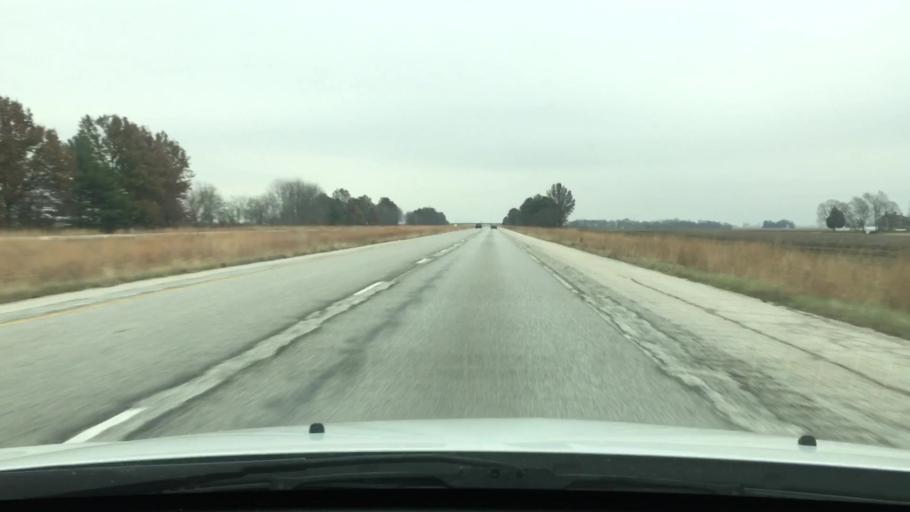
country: US
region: Illinois
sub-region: Morgan County
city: Jacksonville
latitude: 39.7375
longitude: -90.1446
